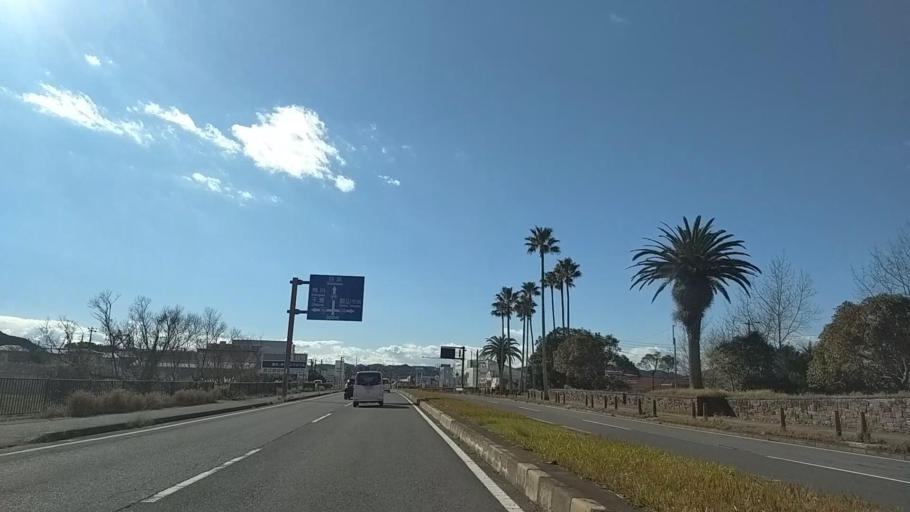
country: JP
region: Chiba
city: Tateyama
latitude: 34.9947
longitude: 139.8744
